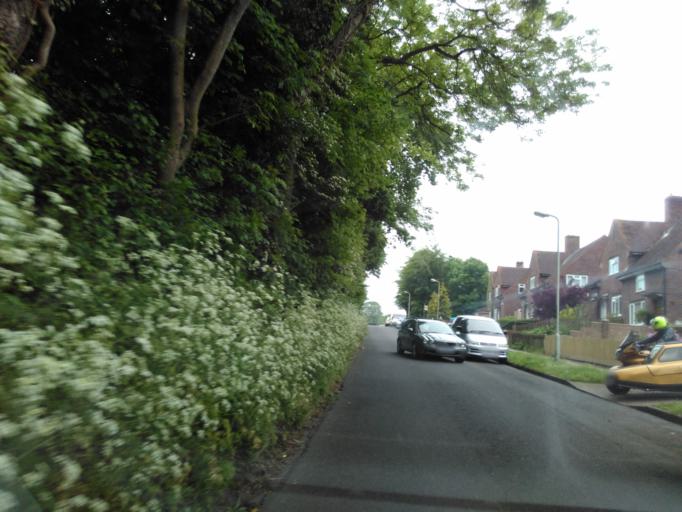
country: GB
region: England
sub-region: Kent
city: Canterbury
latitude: 51.2664
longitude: 1.0572
